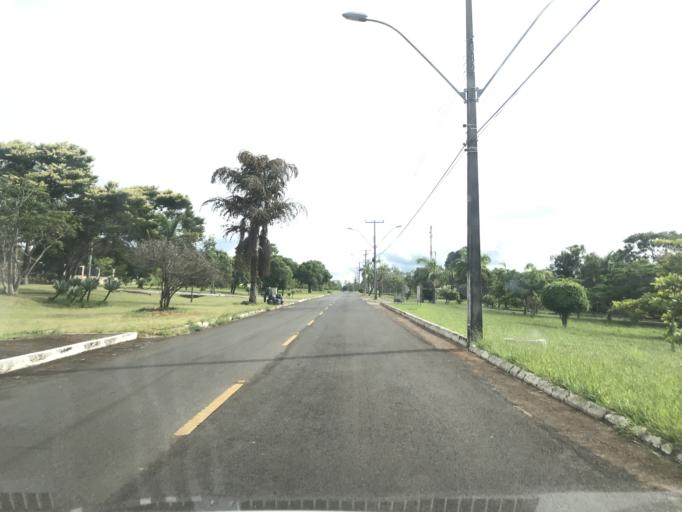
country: BR
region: Federal District
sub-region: Brasilia
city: Brasilia
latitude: -15.8951
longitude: -47.9192
